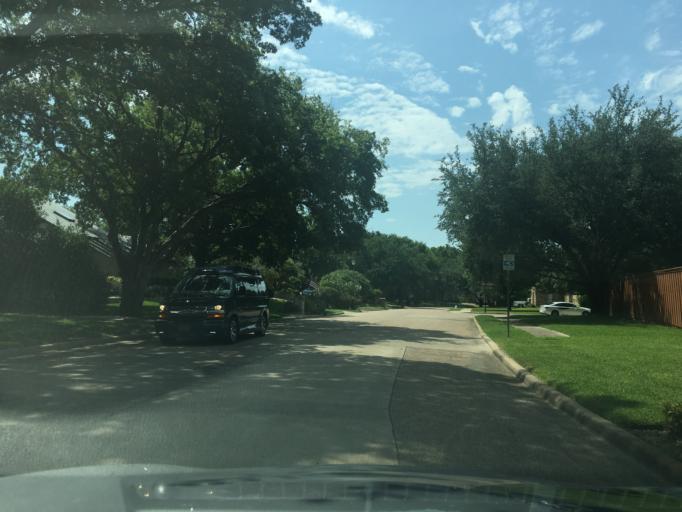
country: US
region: Texas
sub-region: Dallas County
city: Farmers Branch
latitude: 32.9290
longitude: -96.8623
